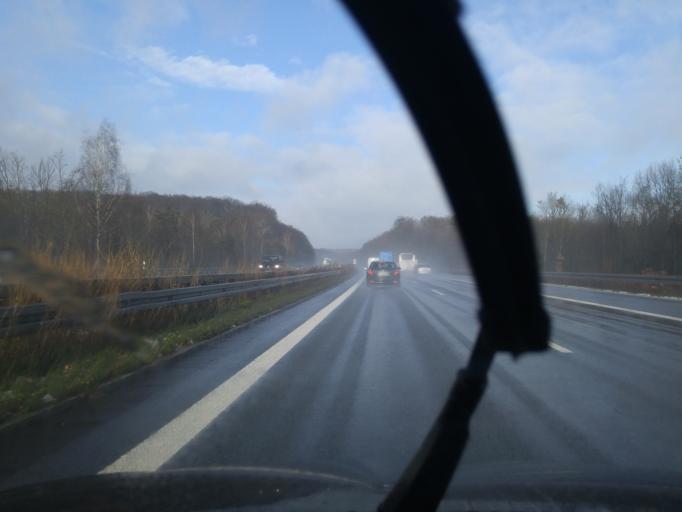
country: DE
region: Bavaria
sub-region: Regierungsbezirk Unterfranken
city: Unterpleichfeld
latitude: 49.9009
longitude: 10.0012
